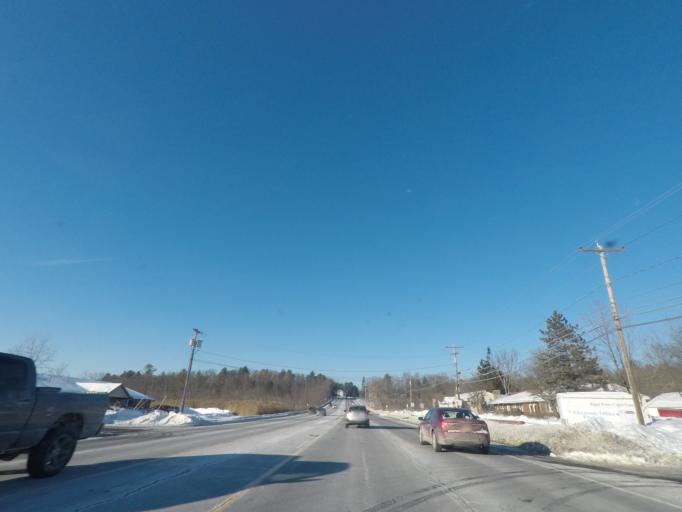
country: US
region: New York
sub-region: Saratoga County
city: Saratoga Springs
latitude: 43.0385
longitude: -73.7900
